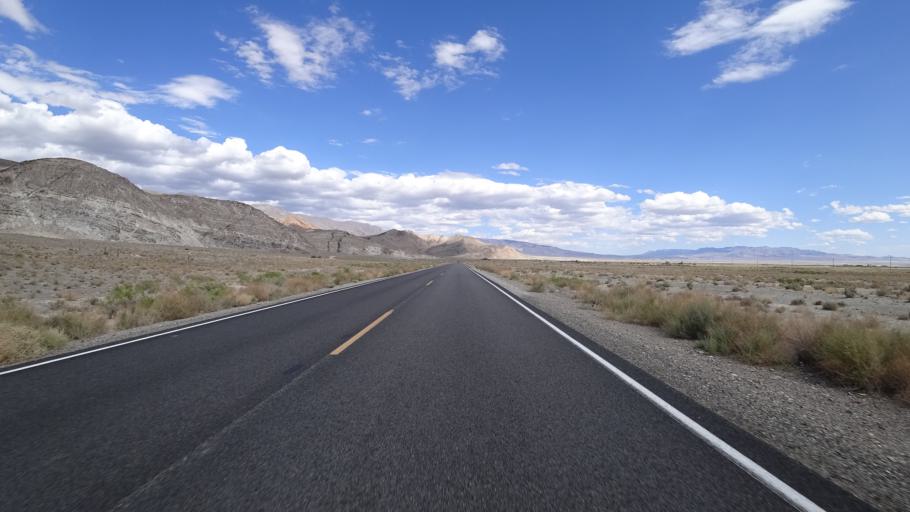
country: US
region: California
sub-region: Inyo County
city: Lone Pine
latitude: 36.5336
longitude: -117.9203
